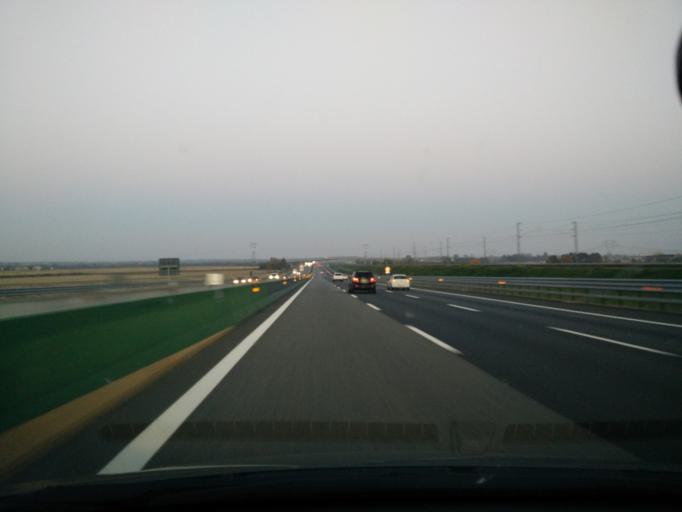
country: IT
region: Piedmont
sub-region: Provincia di Vercelli
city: Balocco
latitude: 45.4403
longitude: 8.2461
